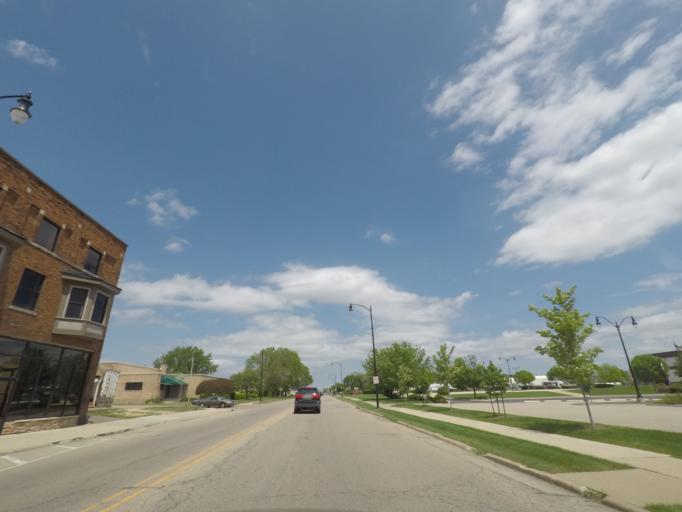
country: US
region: Wisconsin
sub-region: Rock County
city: Beloit
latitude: 42.5030
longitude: -89.0379
